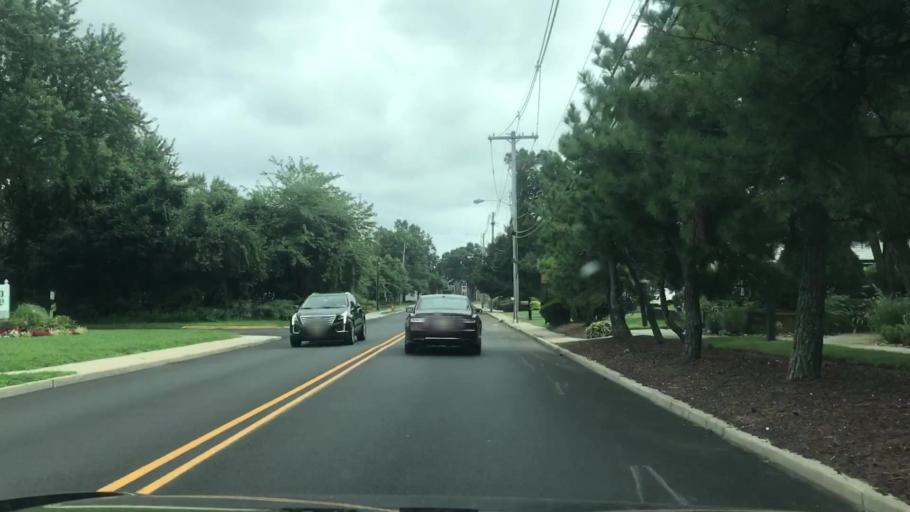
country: US
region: New Jersey
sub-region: Monmouth County
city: Monmouth Beach
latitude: 40.3253
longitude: -73.9920
